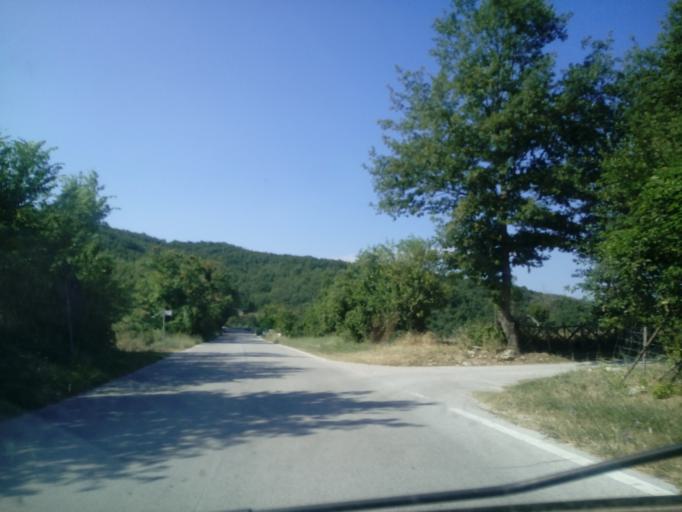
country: IT
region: Molise
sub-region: Provincia di Campobasso
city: Gildone
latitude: 41.5179
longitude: 14.7512
